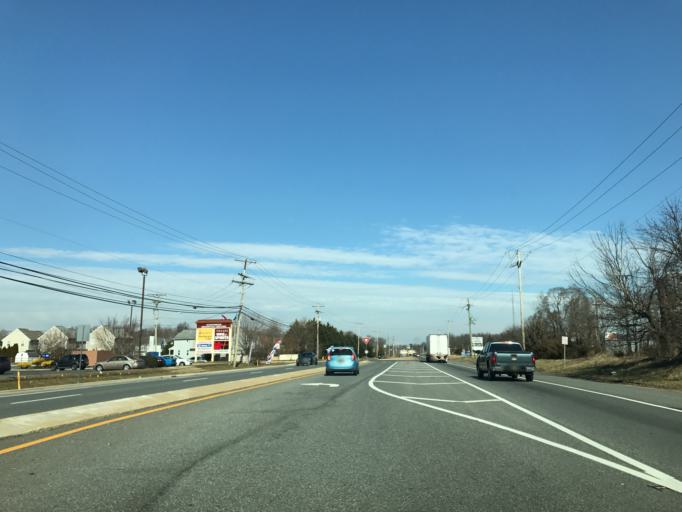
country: US
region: Delaware
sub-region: New Castle County
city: Middletown
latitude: 39.4582
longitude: -75.7224
